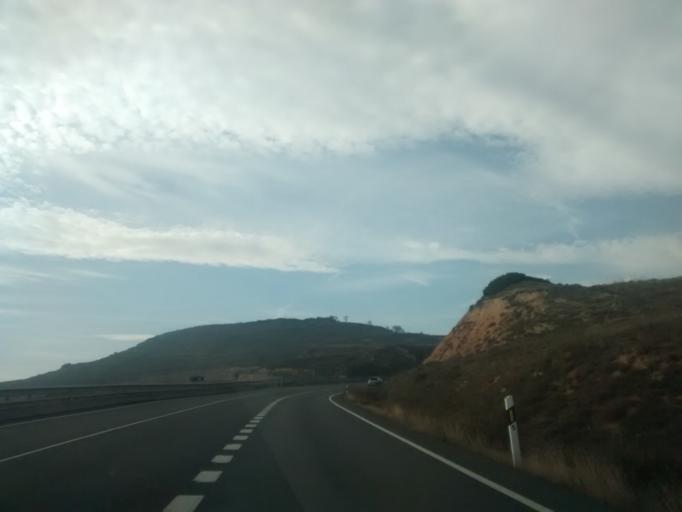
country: ES
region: La Rioja
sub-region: Provincia de La Rioja
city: Cenicero
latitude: 42.4662
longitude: -2.6193
